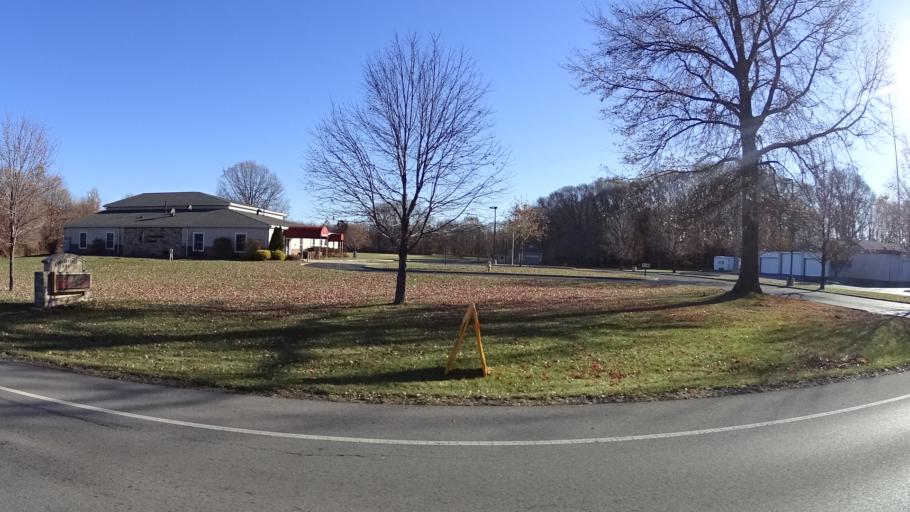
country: US
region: Ohio
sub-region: Lorain County
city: Sheffield
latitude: 41.4158
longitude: -82.1136
